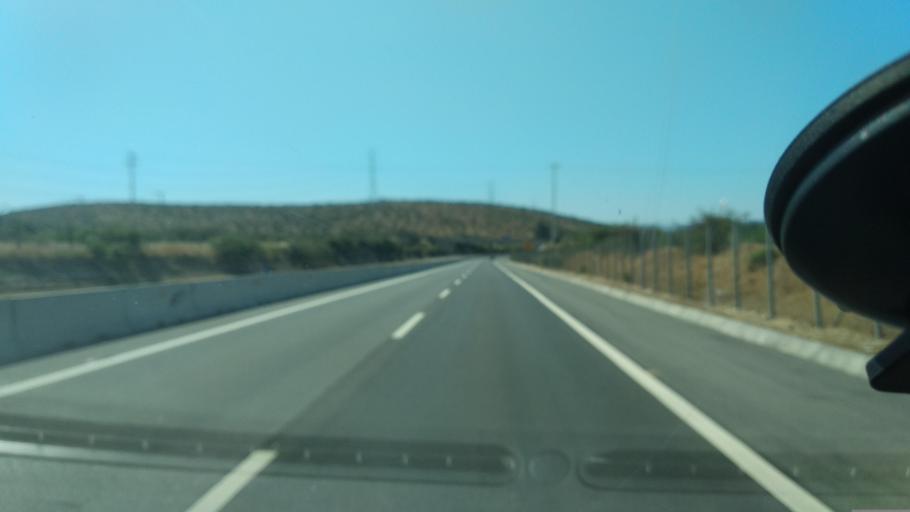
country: CL
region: Valparaiso
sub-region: Provincia de Marga Marga
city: Villa Alemana
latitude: -33.0079
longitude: -71.3264
